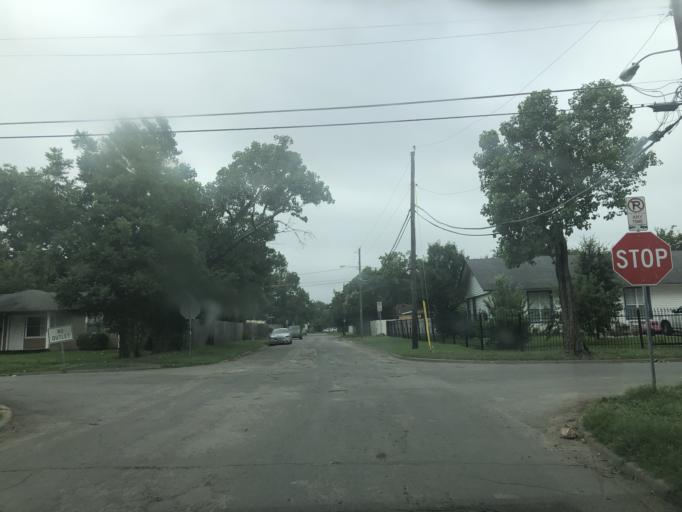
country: US
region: Texas
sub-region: Dallas County
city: Farmers Branch
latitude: 32.8655
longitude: -96.8693
